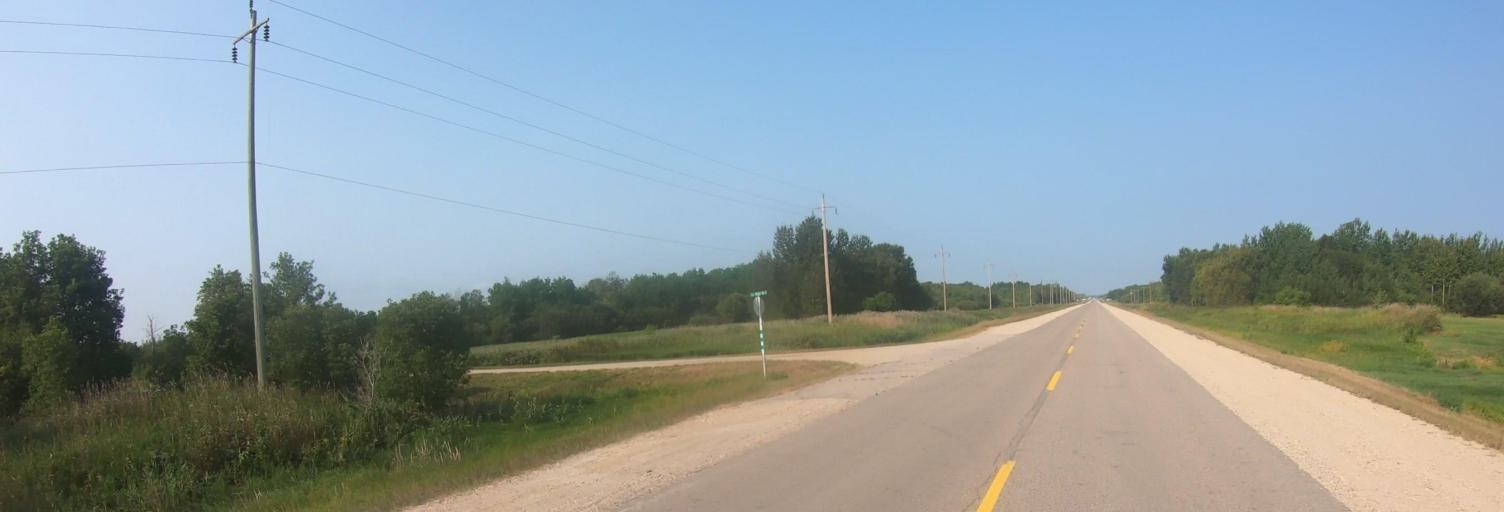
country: US
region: Minnesota
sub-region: Roseau County
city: Roseau
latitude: 49.0234
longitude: -95.6205
